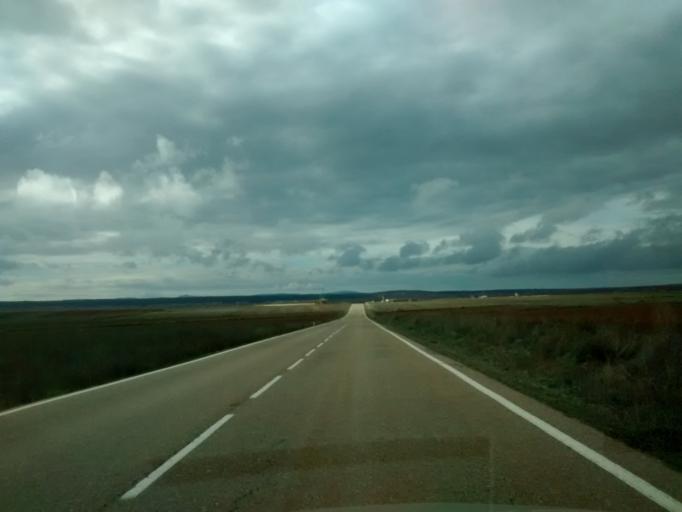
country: ES
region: Aragon
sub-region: Provincia de Zaragoza
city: Used
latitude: 40.9954
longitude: -1.5726
